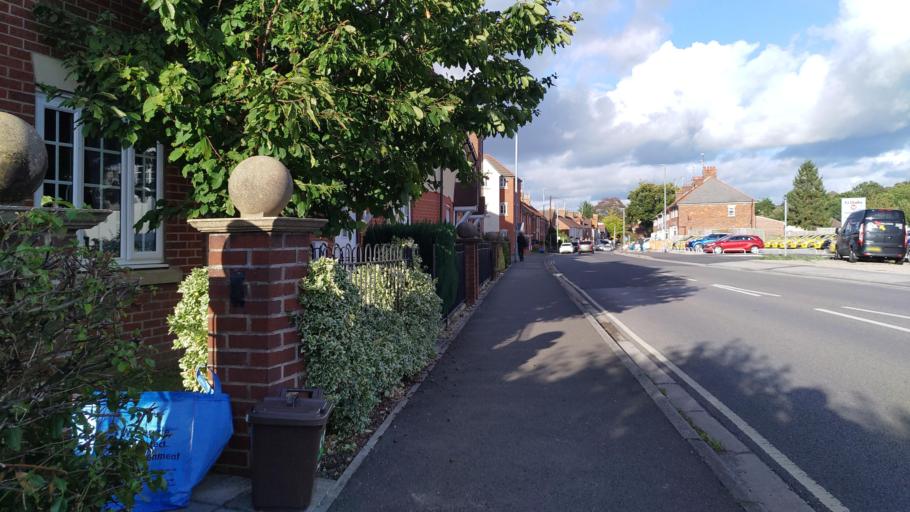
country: GB
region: England
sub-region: Somerset
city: Yeovil
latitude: 50.9372
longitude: -2.6428
